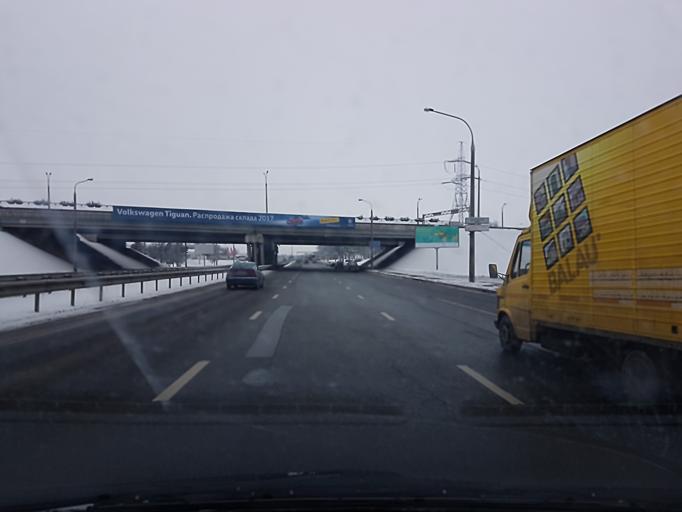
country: BY
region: Minsk
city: Shchomyslitsa
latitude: 53.8433
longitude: 27.4699
